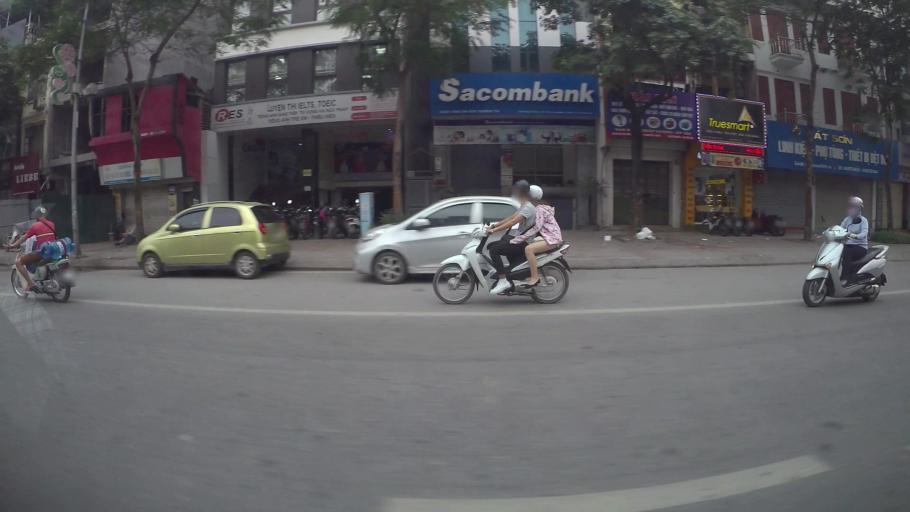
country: VN
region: Ha Noi
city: Hoan Kiem
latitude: 21.0477
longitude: 105.8801
